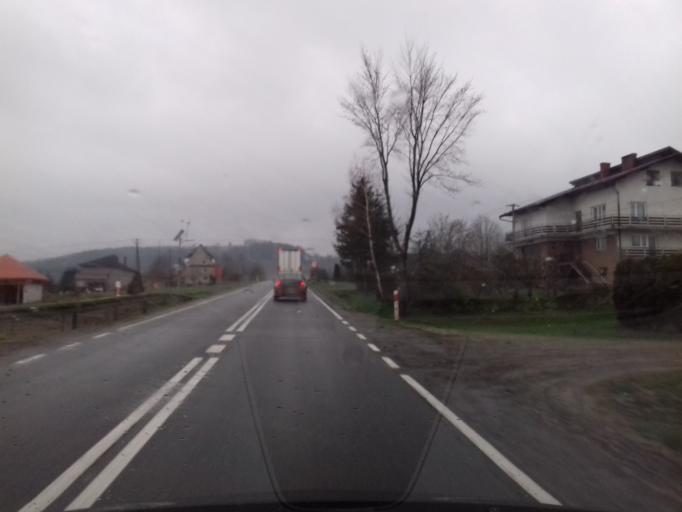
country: PL
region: Lesser Poland Voivodeship
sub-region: Powiat nowosadecki
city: Chelmiec
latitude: 49.6487
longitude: 20.6063
